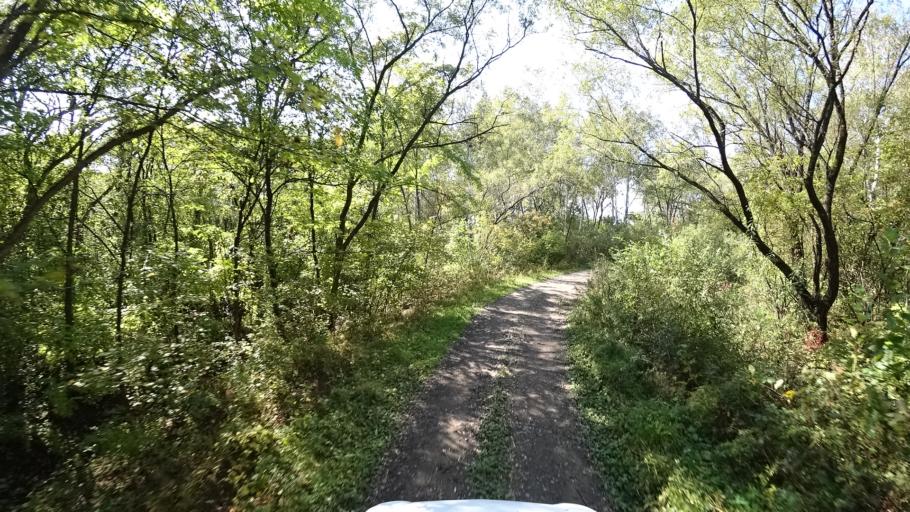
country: RU
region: Amur
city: Arkhara
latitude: 49.3999
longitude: 130.1231
